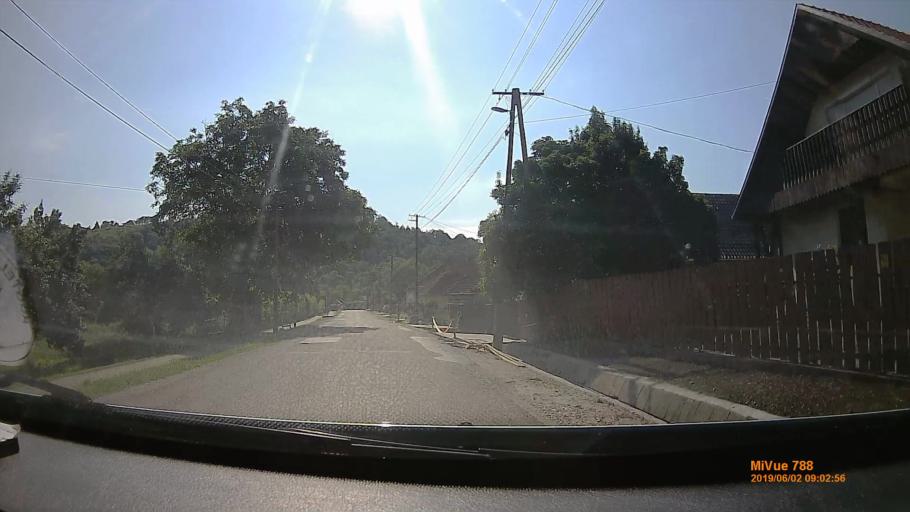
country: HU
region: Borsod-Abauj-Zemplen
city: Kazincbarcika
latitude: 48.1656
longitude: 20.6369
